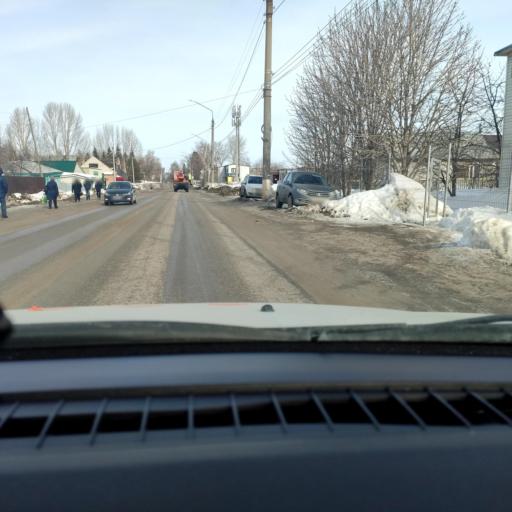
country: RU
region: Samara
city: Kinel'
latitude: 53.2335
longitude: 50.6310
